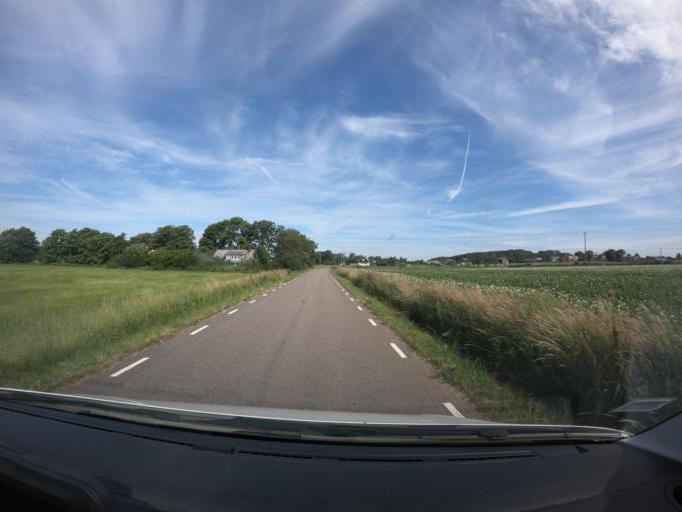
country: SE
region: Skane
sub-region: Angelholms Kommun
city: Vejbystrand
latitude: 56.4033
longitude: 12.6639
